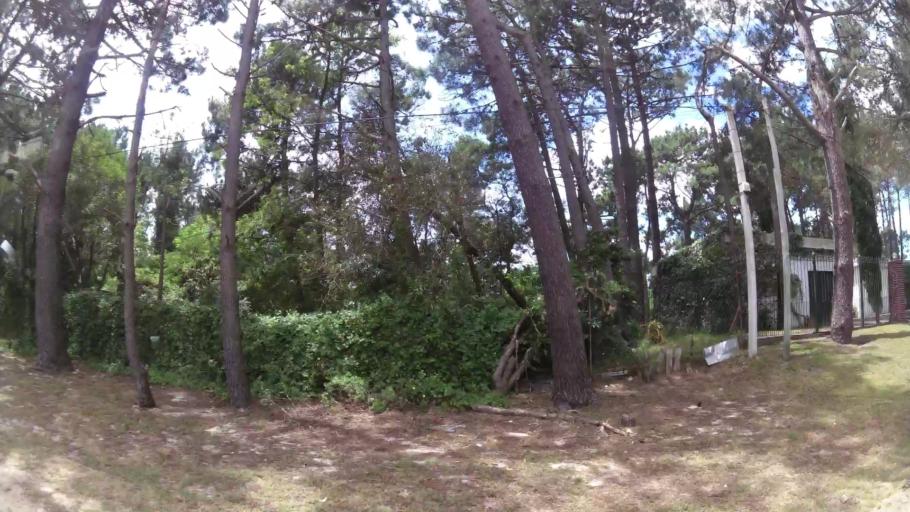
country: UY
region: Canelones
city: Pando
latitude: -34.7958
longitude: -55.8969
